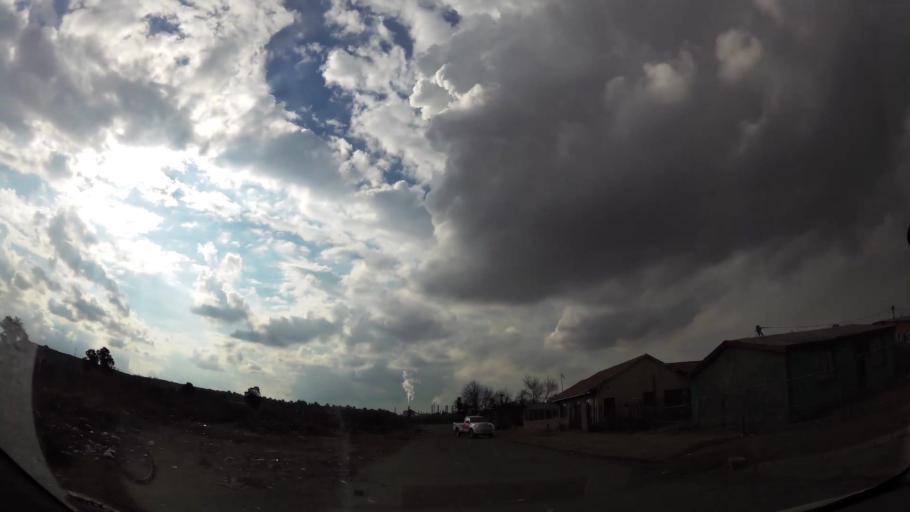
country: ZA
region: Orange Free State
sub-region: Fezile Dabi District Municipality
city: Sasolburg
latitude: -26.8413
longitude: 27.8401
